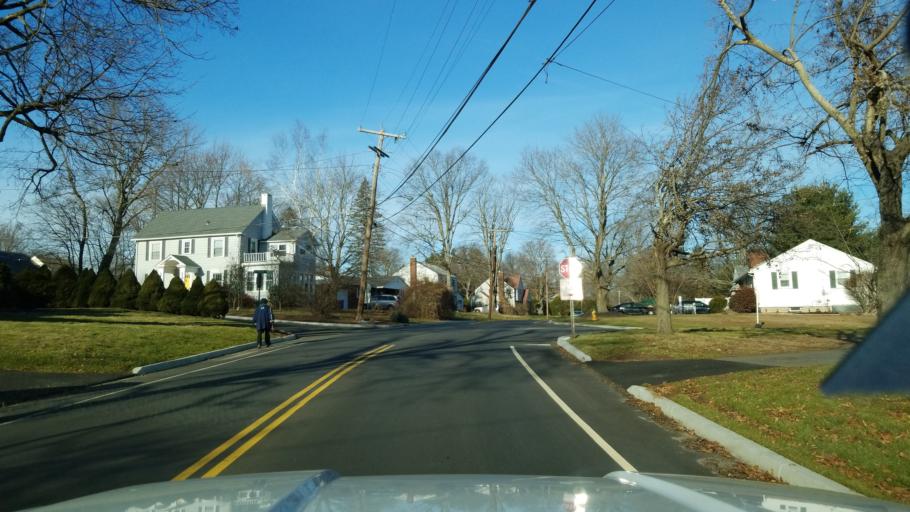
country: US
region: Connecticut
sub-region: Middlesex County
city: Middletown
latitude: 41.5574
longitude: -72.6757
